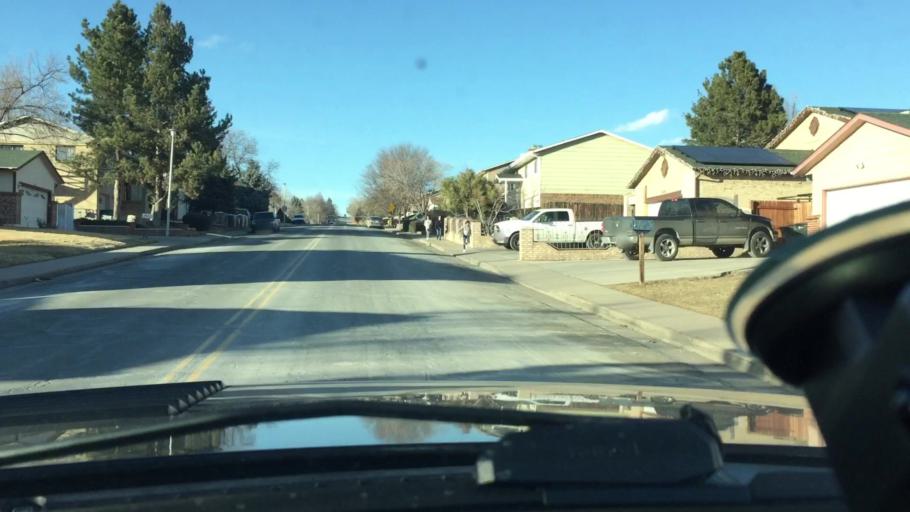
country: US
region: Colorado
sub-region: Adams County
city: Federal Heights
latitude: 39.8714
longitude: -105.0056
